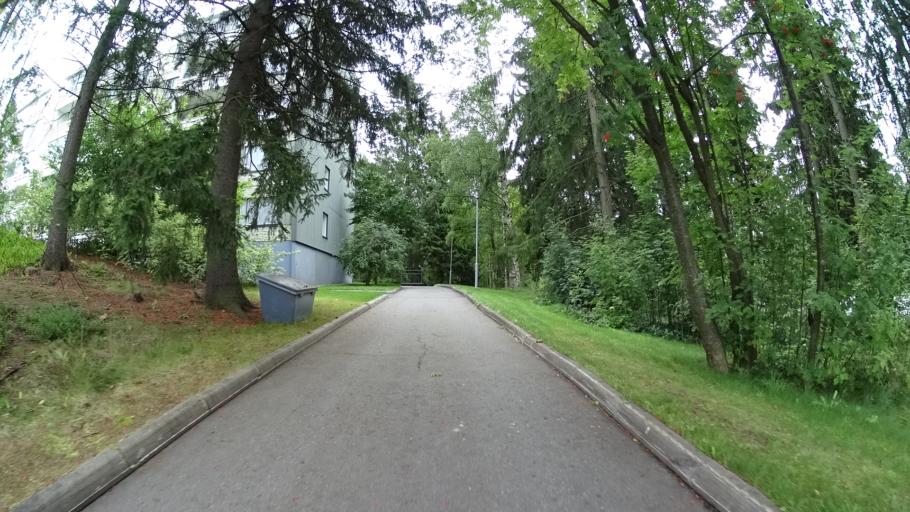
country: FI
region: Uusimaa
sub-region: Helsinki
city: Teekkarikylae
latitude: 60.2696
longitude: 24.8581
